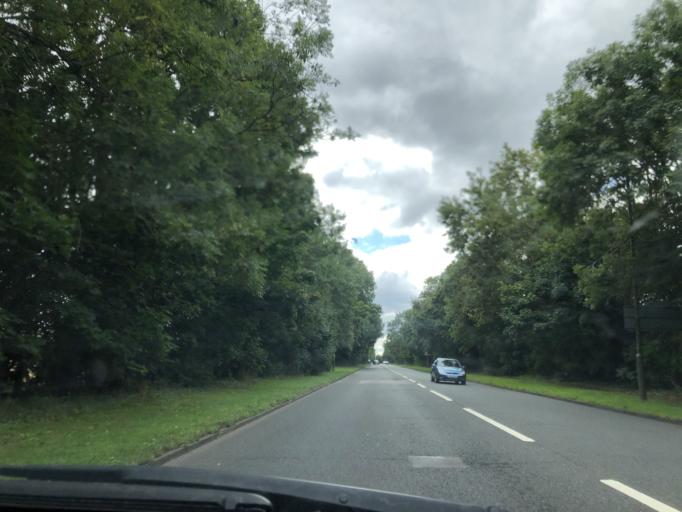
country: GB
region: England
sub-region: Kent
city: Halstead
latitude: 51.3552
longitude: 0.1266
